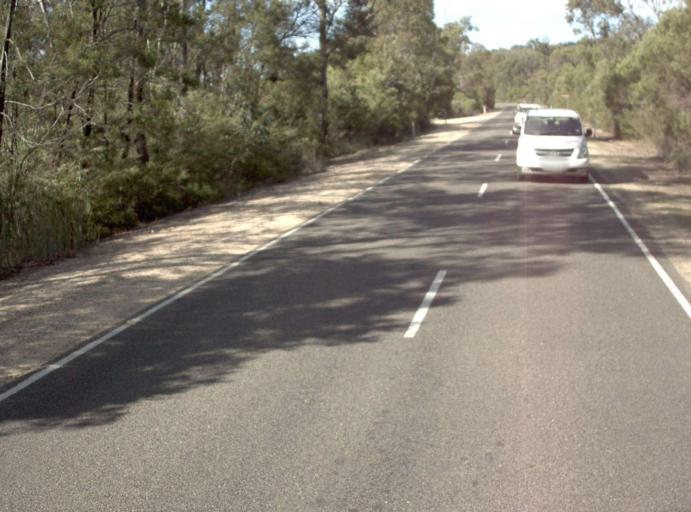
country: AU
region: Victoria
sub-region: East Gippsland
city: Lakes Entrance
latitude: -37.5774
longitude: 148.1259
